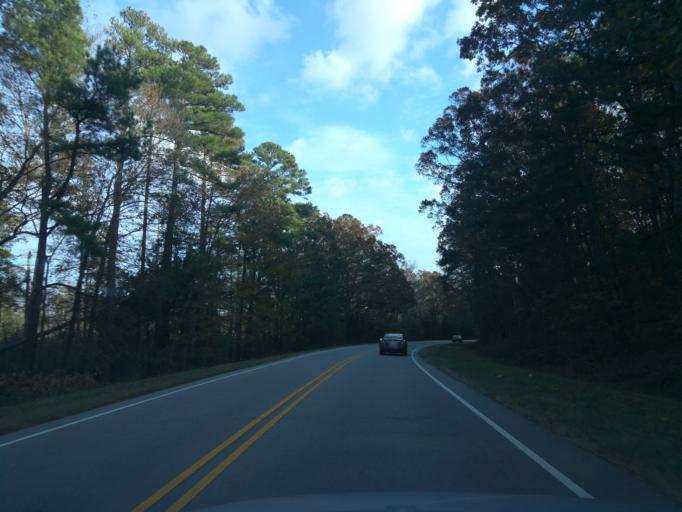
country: US
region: North Carolina
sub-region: Durham County
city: Durham
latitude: 36.0206
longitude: -78.9857
